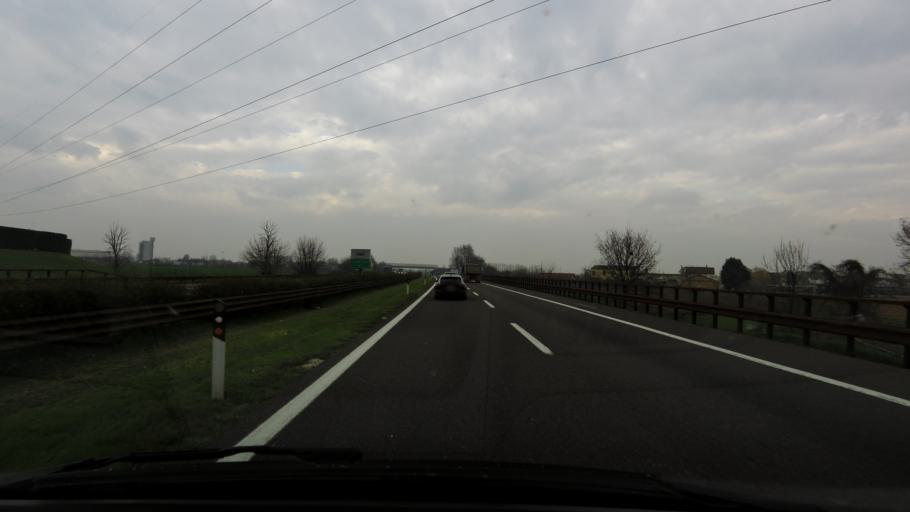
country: IT
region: Lombardy
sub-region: Provincia di Mantova
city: Stradella
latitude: 45.1340
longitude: 10.8714
